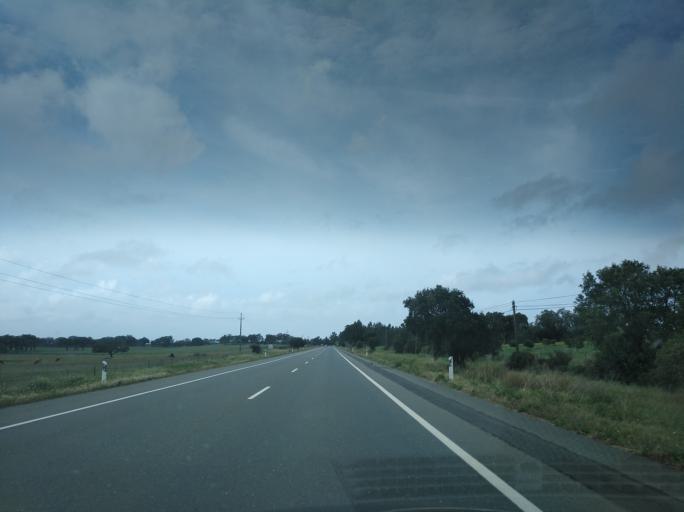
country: PT
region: Setubal
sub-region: Grandola
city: Grandola
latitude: 38.1509
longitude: -8.5131
